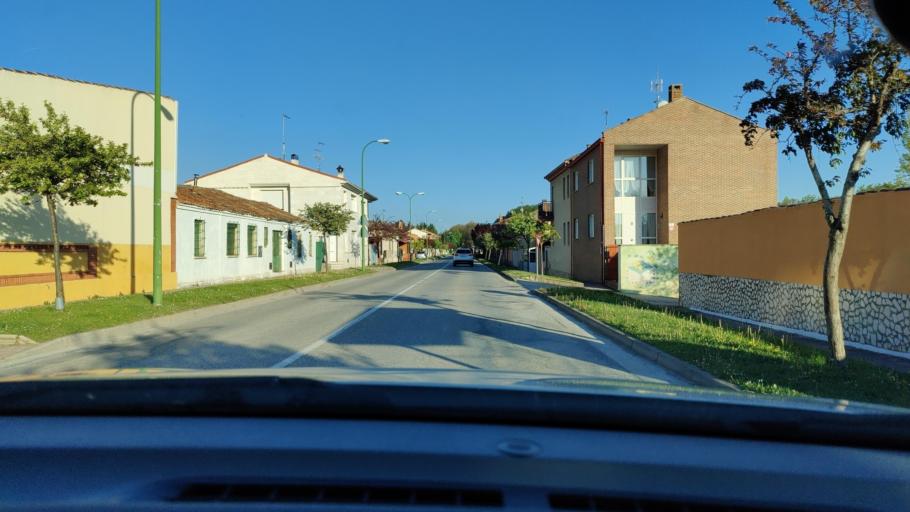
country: ES
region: Castille and Leon
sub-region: Provincia de Burgos
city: Villalbilla de Burgos
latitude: 42.3489
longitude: -3.7335
